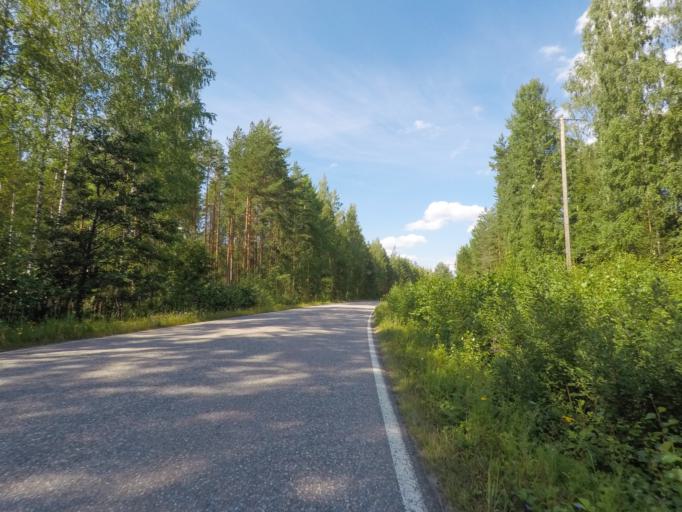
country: FI
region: Southern Savonia
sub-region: Mikkeli
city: Puumala
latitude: 61.4864
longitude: 28.1663
